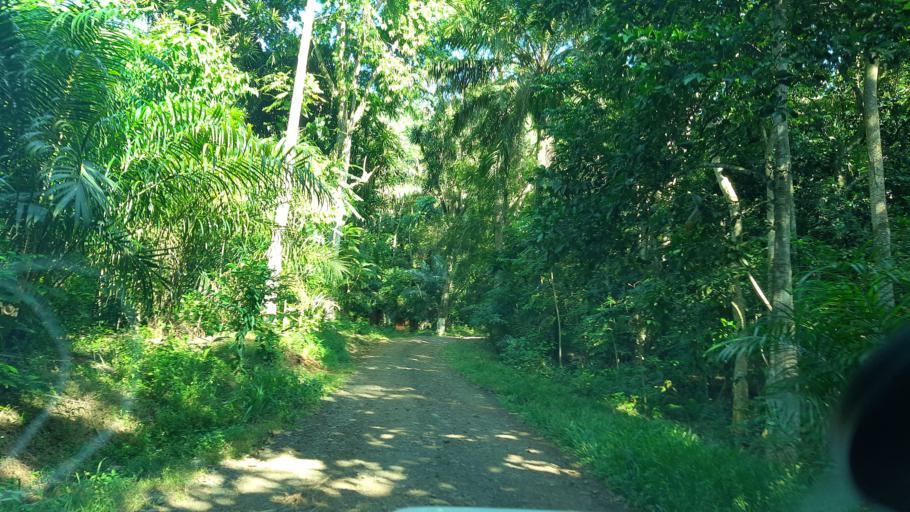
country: ST
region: Sao Tome Island
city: Sao Tome
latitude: 0.2434
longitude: 6.7417
